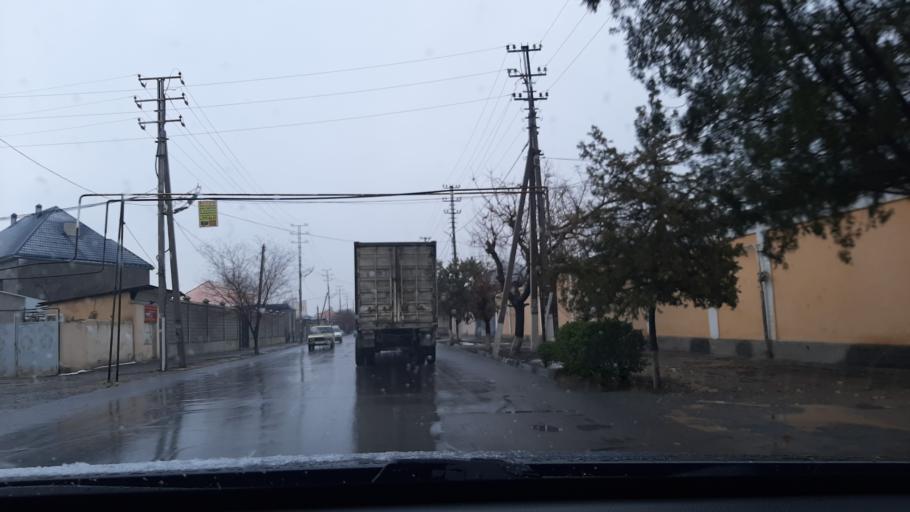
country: TJ
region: Viloyati Sughd
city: Khujand
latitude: 40.2698
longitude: 69.6310
